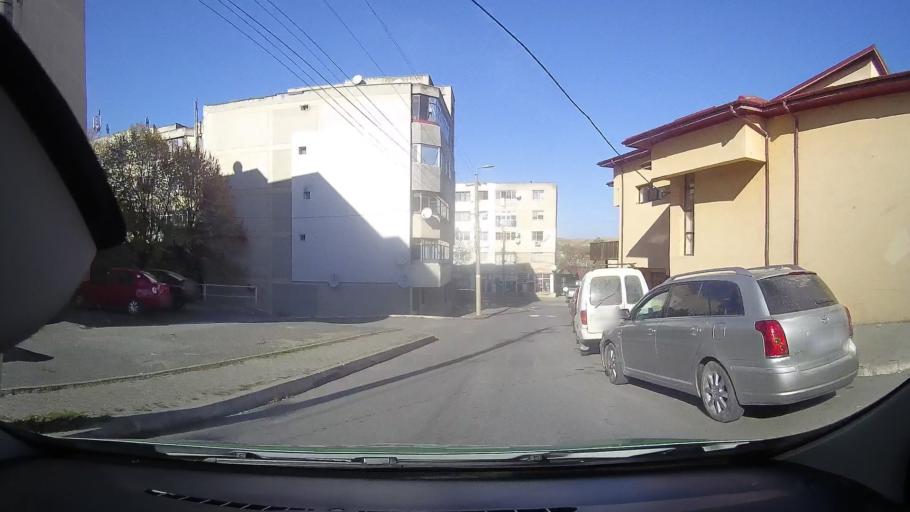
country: RO
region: Tulcea
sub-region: Oras Babadag
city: Babadag
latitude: 44.8939
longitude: 28.7252
